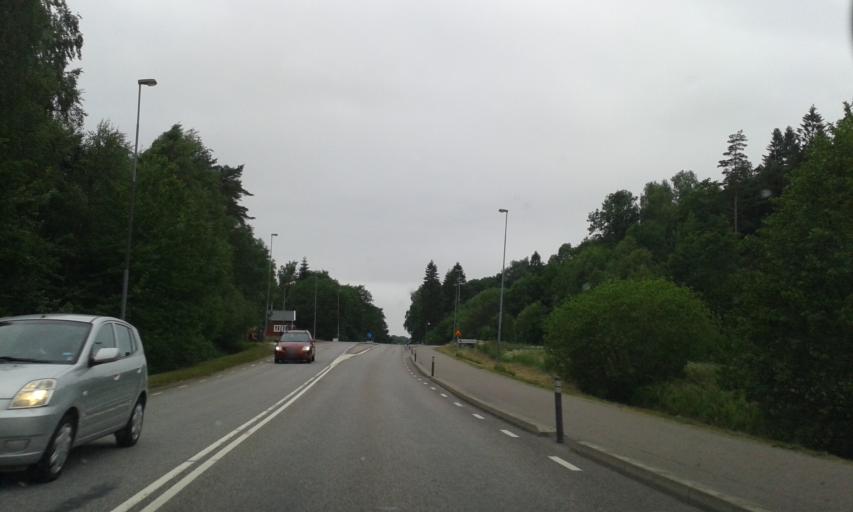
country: SE
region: Vaestra Goetaland
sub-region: Kungalvs Kommun
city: Kungalv
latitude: 57.8889
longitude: 11.9579
